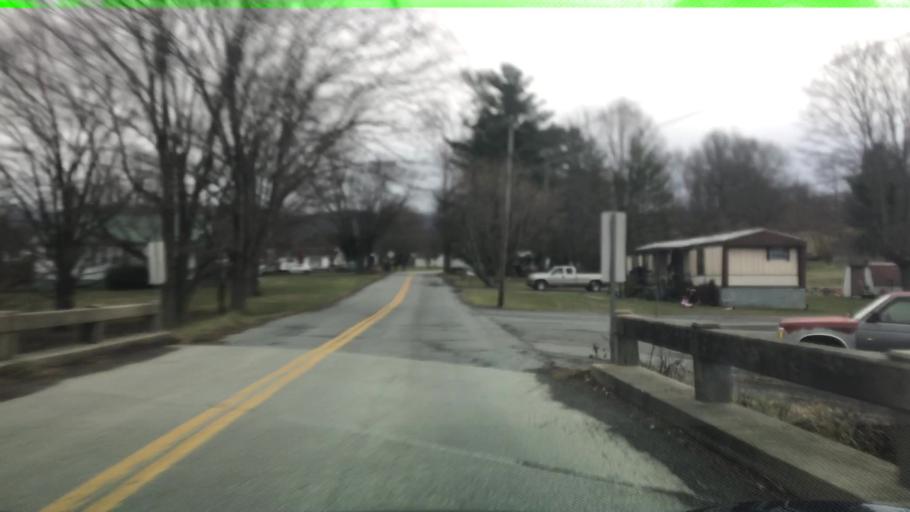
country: US
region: Virginia
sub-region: Smyth County
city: Atkins
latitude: 36.7742
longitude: -81.4108
